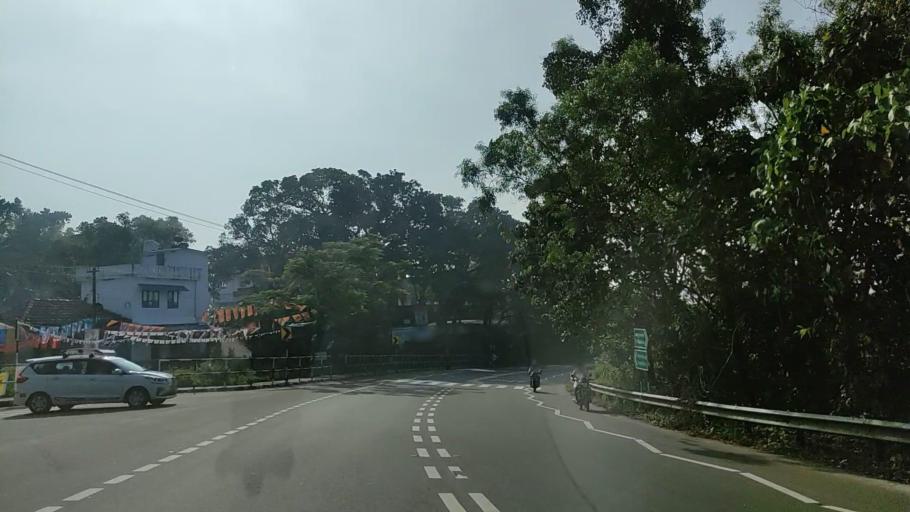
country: IN
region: Kerala
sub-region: Kollam
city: Punalur
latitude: 8.9784
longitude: 76.8141
